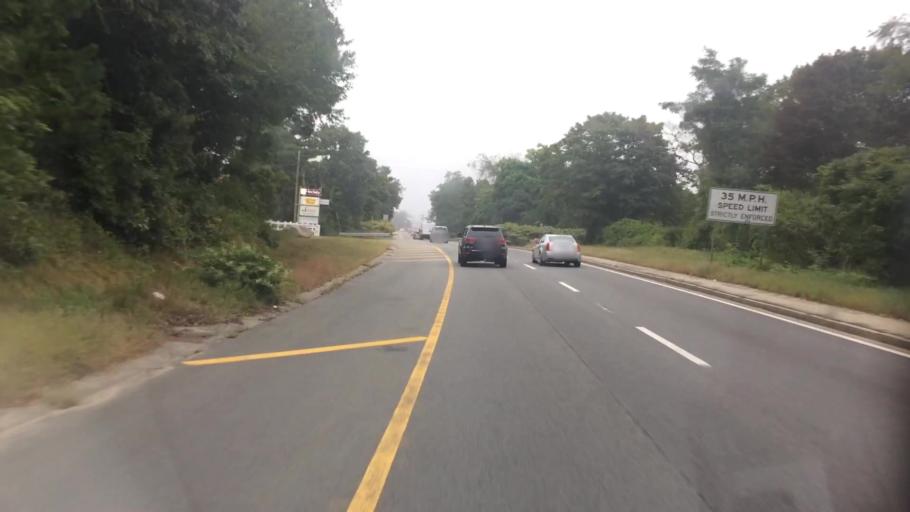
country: US
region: Massachusetts
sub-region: Plymouth County
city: Onset
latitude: 41.7601
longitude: -70.6723
